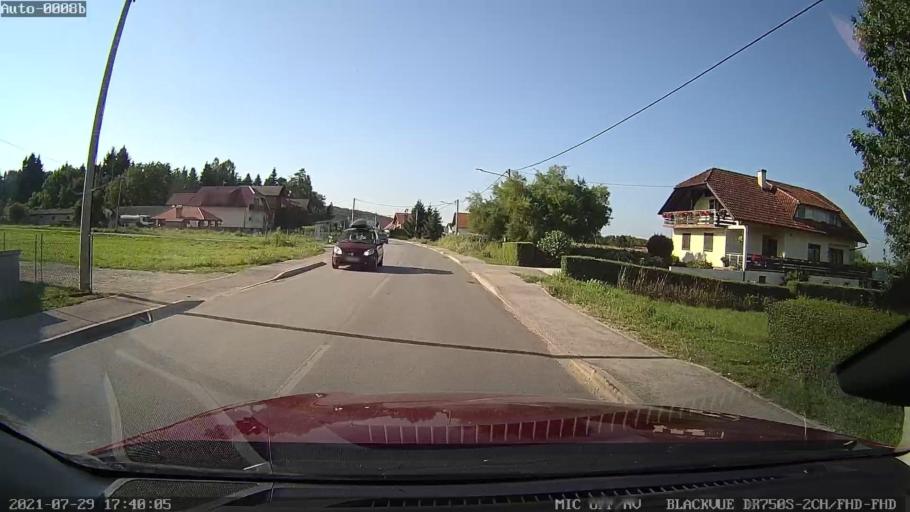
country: HR
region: Varazdinska
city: Vinica
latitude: 46.3199
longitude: 16.1561
